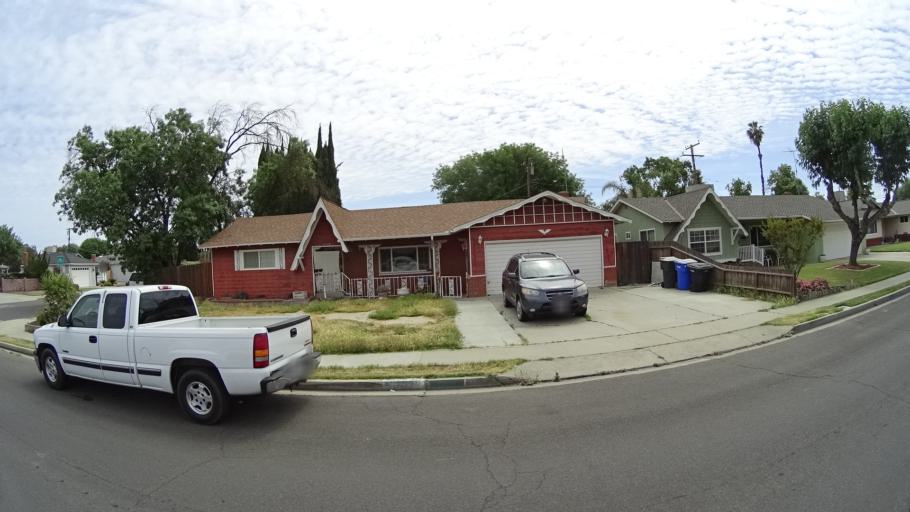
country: US
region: California
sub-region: Kings County
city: Hanford
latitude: 36.3492
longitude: -119.6416
